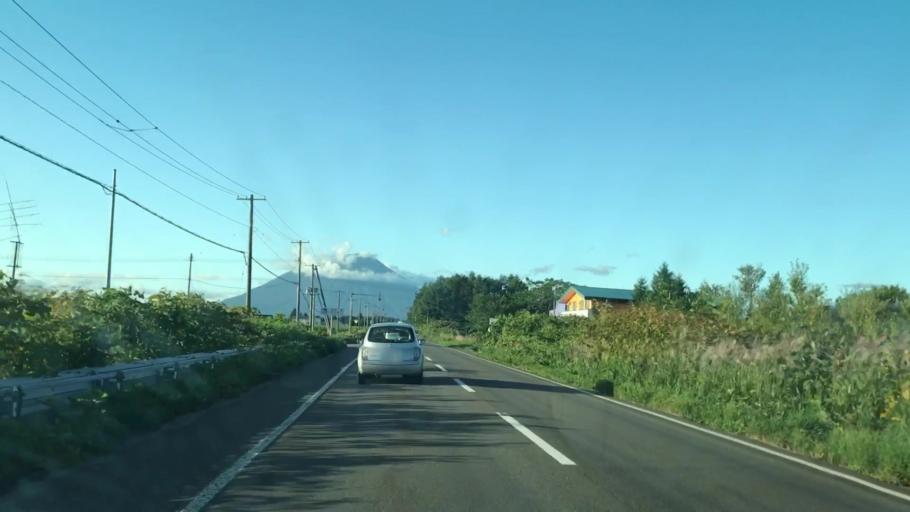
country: JP
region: Hokkaido
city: Niseko Town
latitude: 42.6529
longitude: 140.8111
